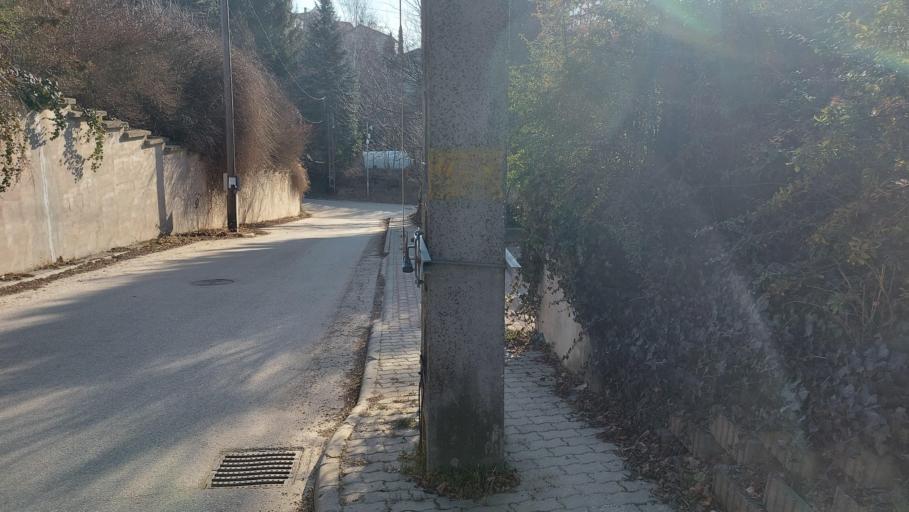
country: HU
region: Pest
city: Budaors
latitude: 47.4628
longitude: 18.9269
